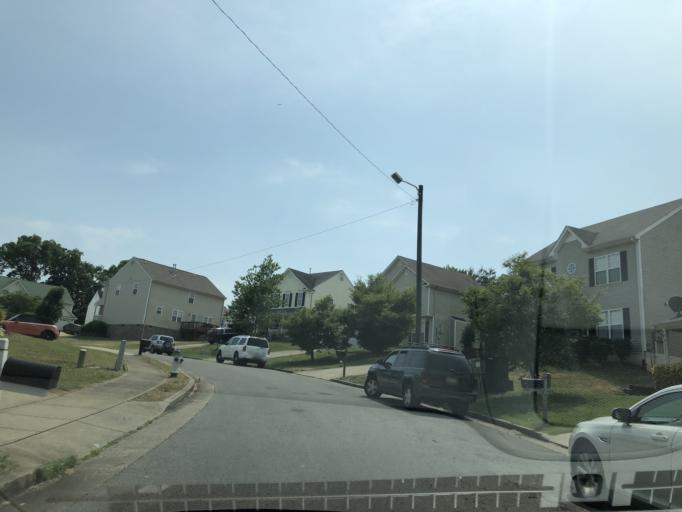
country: US
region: Tennessee
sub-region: Rutherford County
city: La Vergne
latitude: 36.0488
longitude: -86.6166
